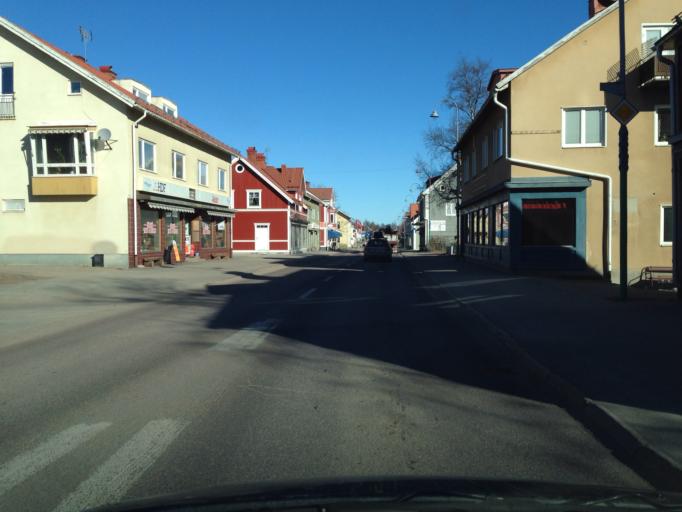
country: SE
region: Gaevleborg
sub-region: Ljusdals Kommun
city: Jaervsoe
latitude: 61.7138
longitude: 16.1691
